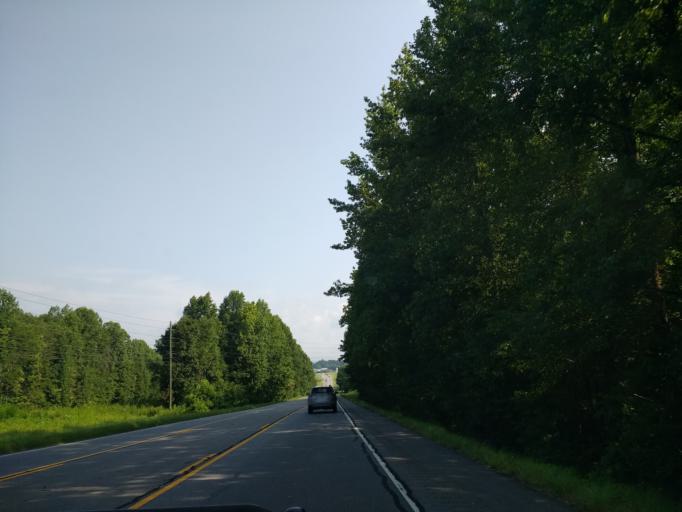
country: US
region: Georgia
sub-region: White County
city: Cleveland
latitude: 34.5475
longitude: -83.7606
